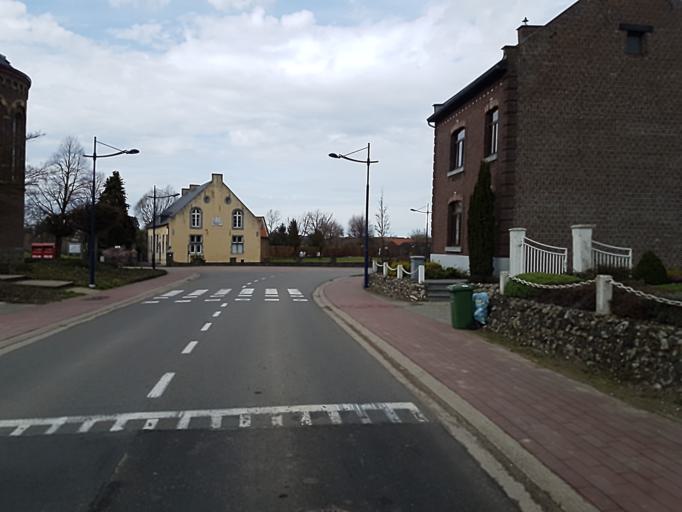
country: BE
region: Flanders
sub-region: Provincie Limburg
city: Nieuwerkerken
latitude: 50.8745
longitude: 5.2400
